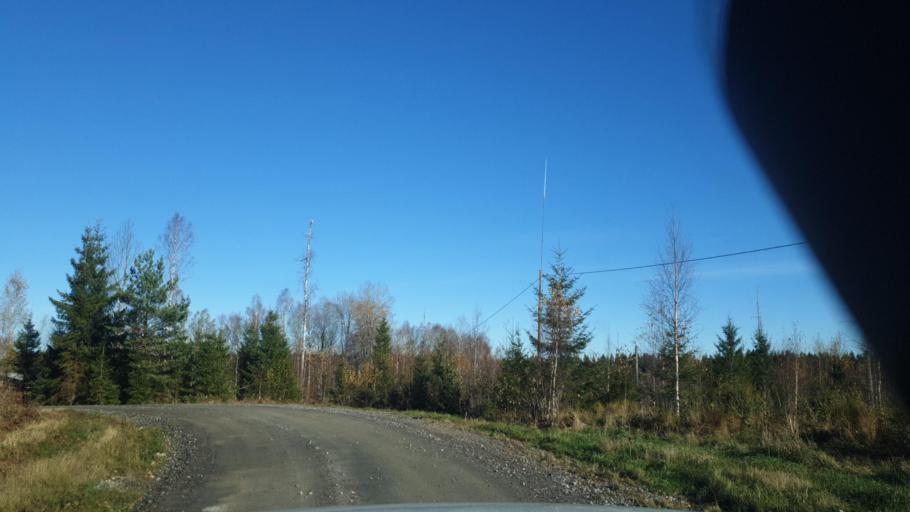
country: SE
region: Vaermland
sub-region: Karlstads Kommun
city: Edsvalla
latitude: 59.4761
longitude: 13.1312
